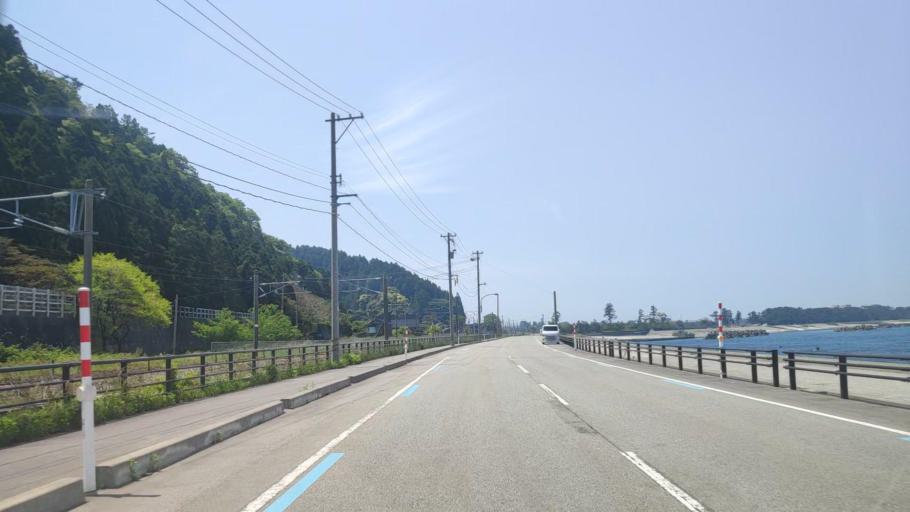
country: JP
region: Toyama
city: Nyuzen
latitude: 36.9667
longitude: 137.5779
